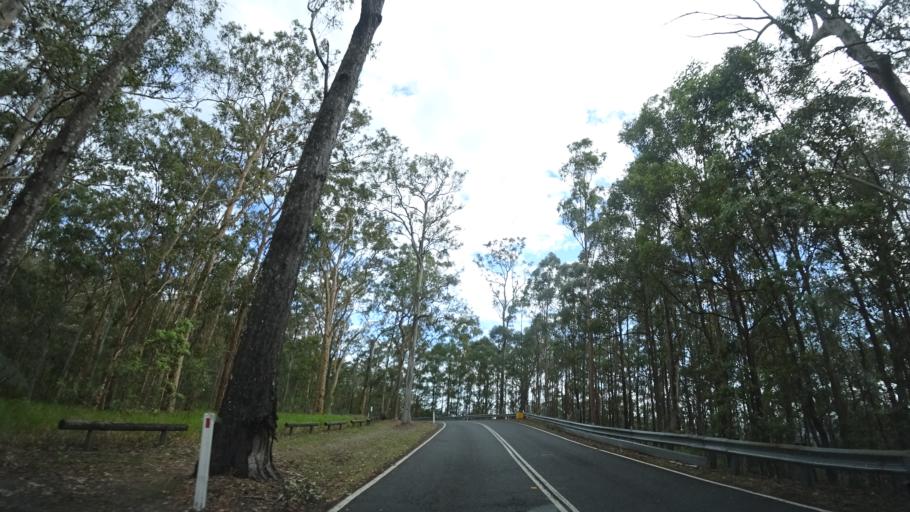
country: AU
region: Queensland
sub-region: Brisbane
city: Kenmore Hills
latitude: -27.4760
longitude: 152.9463
